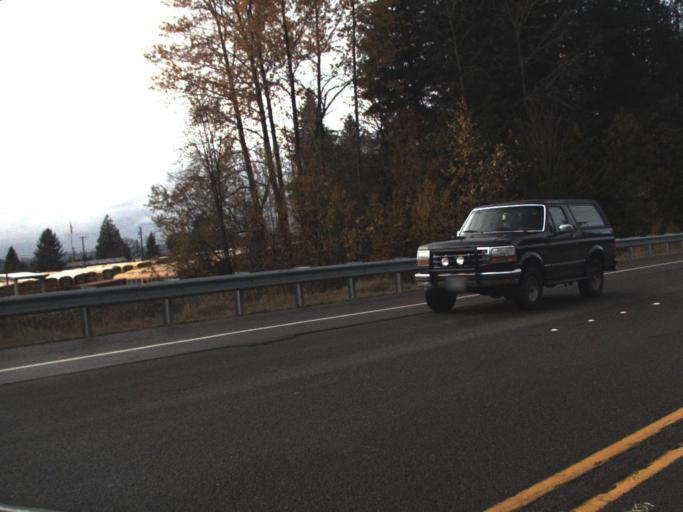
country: US
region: Washington
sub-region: Snohomish County
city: Fobes Hill
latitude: 47.9549
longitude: -122.1152
